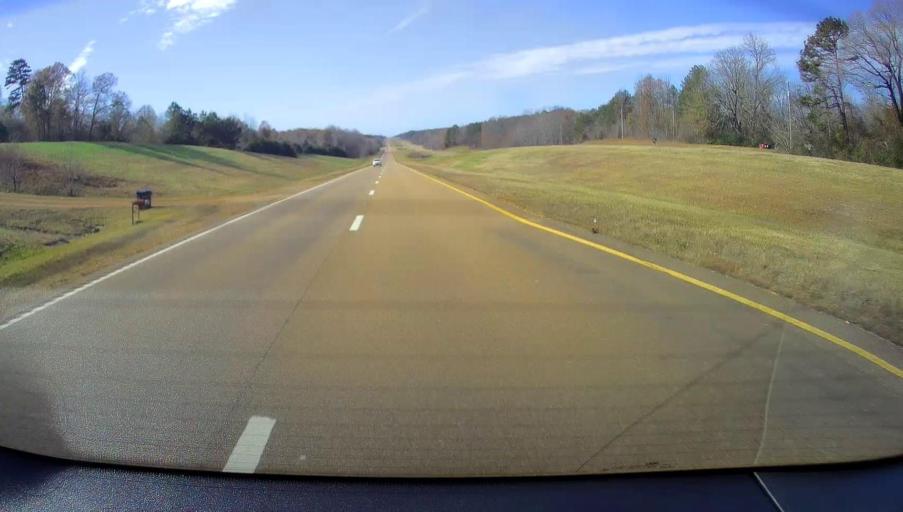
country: US
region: Mississippi
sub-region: Benton County
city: Ashland
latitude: 34.9530
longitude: -89.0471
